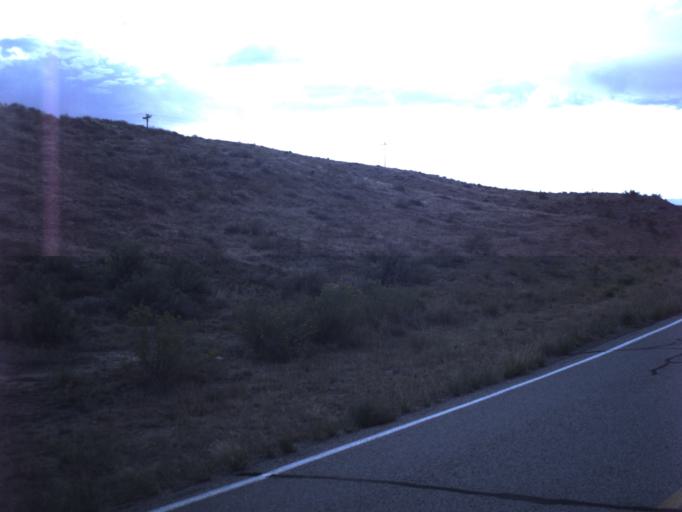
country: US
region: Utah
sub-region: Grand County
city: Moab
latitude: 38.8577
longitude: -109.2904
